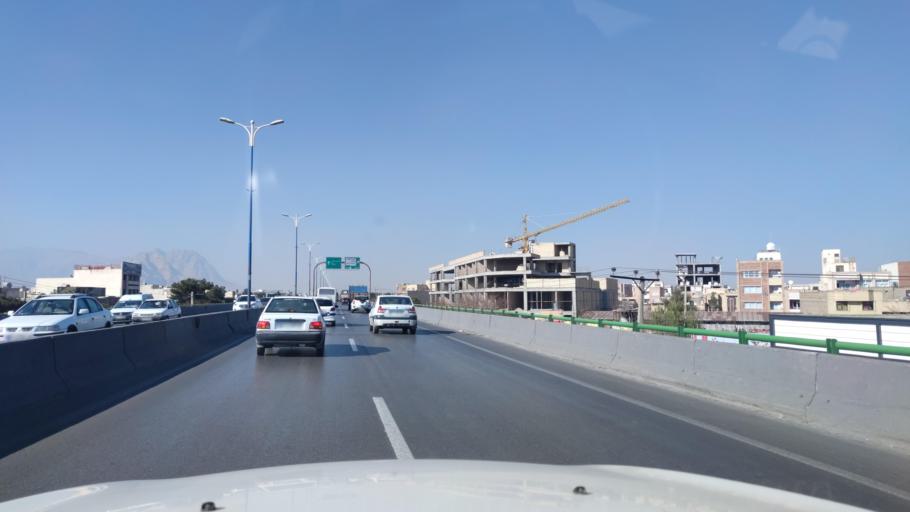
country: IR
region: Isfahan
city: Rehnan
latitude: 32.6976
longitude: 51.6207
